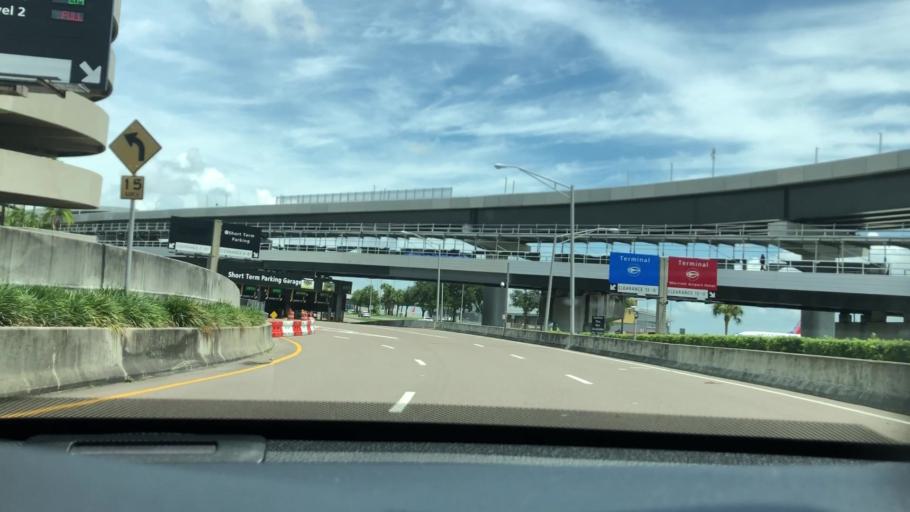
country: US
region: Florida
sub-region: Hillsborough County
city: Egypt Lake-Leto
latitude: 27.9772
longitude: -82.5333
